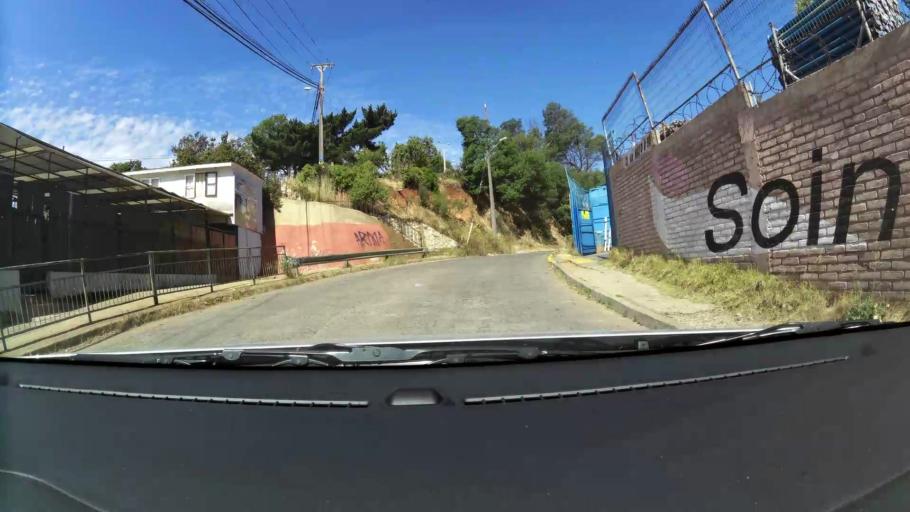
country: CL
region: Valparaiso
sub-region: Provincia de Valparaiso
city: Vina del Mar
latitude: -33.0425
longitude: -71.5701
